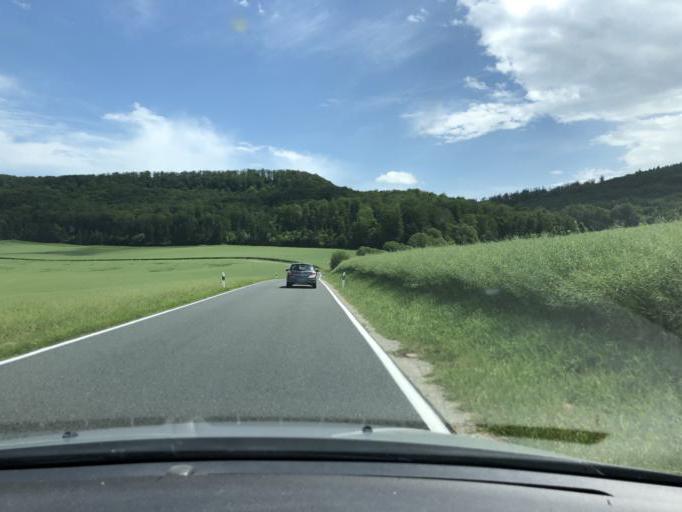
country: DE
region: Thuringia
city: Grossbartloff
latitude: 51.2887
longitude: 10.1978
